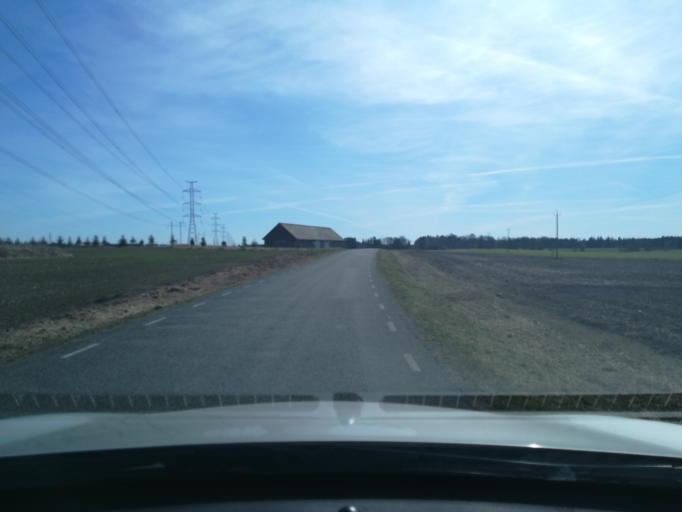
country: EE
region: Harju
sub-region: Saku vald
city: Saku
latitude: 59.2879
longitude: 24.6236
